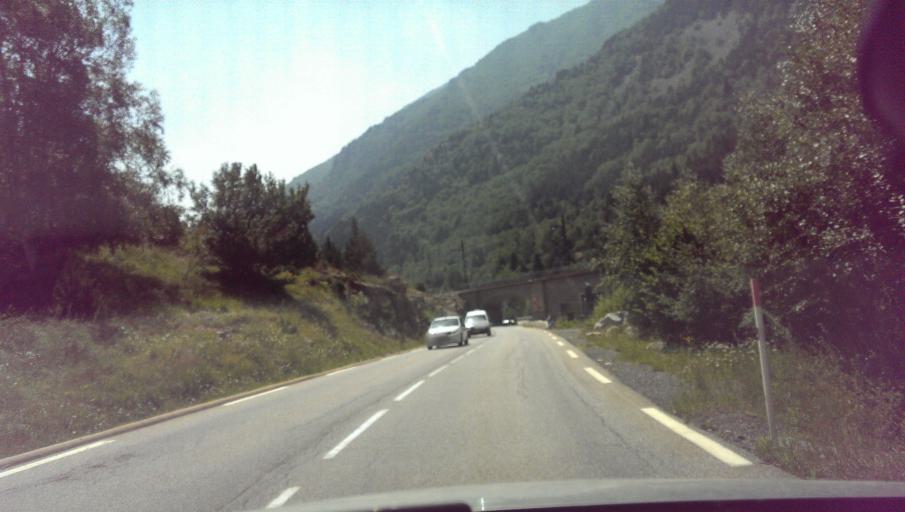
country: ES
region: Catalonia
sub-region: Provincia de Girona
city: Meranges
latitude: 42.5155
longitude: 1.8244
